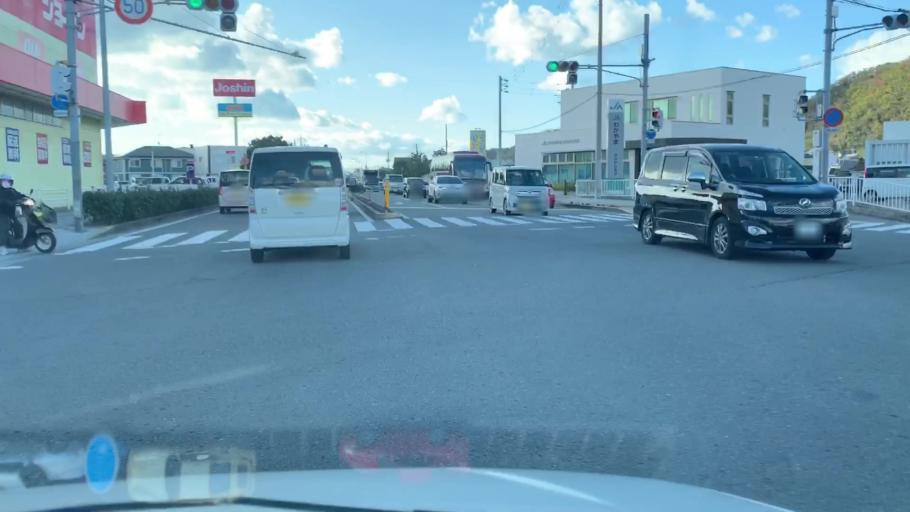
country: JP
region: Wakayama
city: Wakayama-shi
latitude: 34.2595
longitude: 135.1687
